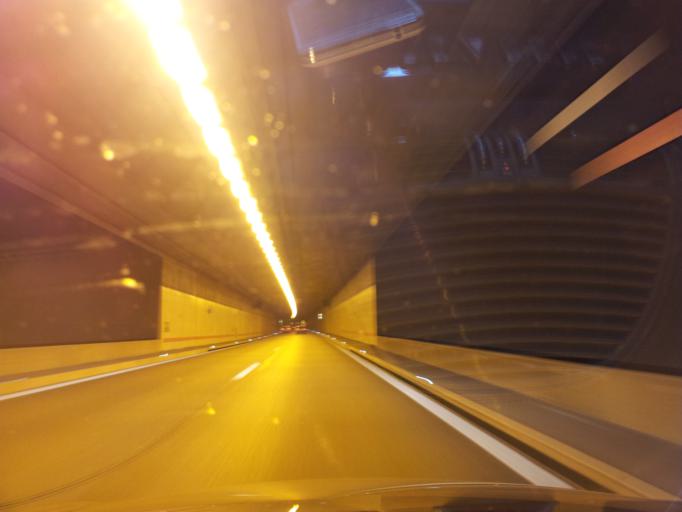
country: CH
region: Solothurn
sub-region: Bezirk Lebern
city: Langendorf
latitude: 47.1948
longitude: 7.5132
